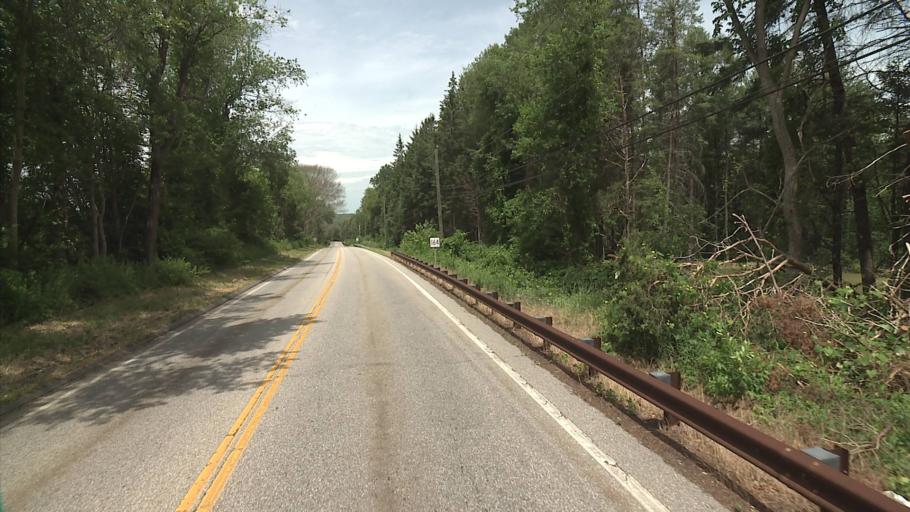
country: US
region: Connecticut
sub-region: New London County
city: Preston City
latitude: 41.5492
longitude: -71.9676
